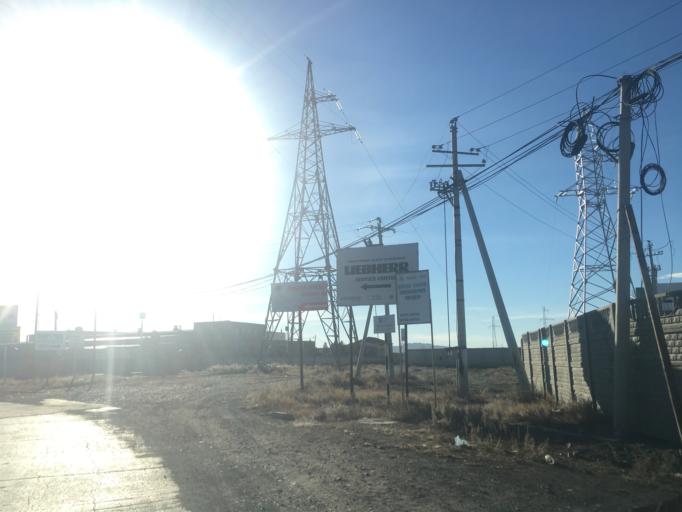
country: MN
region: Ulaanbaatar
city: Ulaanbaatar
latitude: 47.9014
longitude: 106.7973
